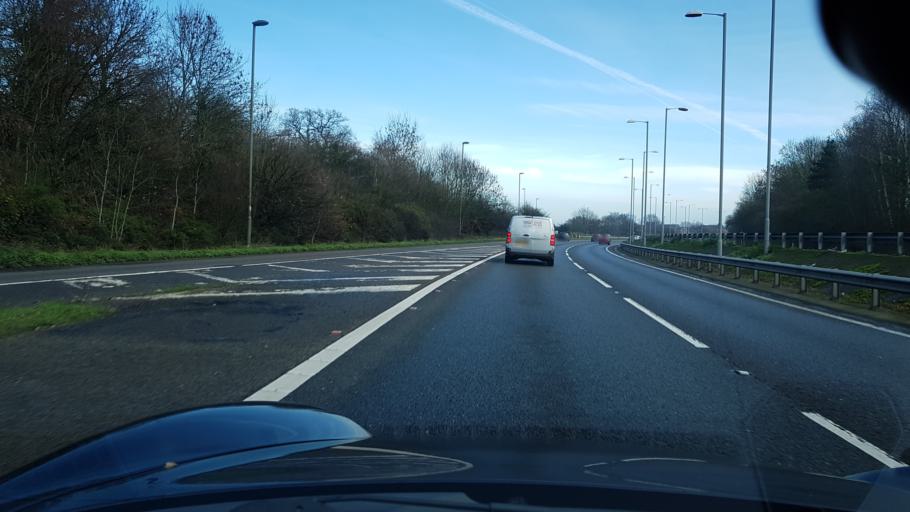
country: GB
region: England
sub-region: Surrey
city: Ditton Hill
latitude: 51.3755
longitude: -0.3134
